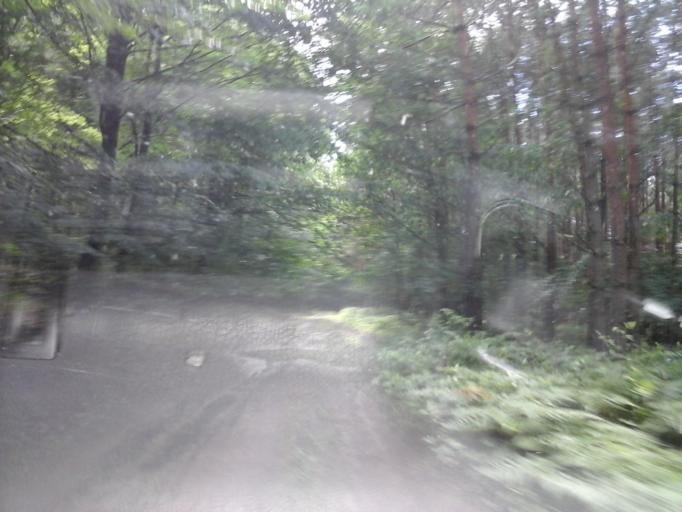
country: PL
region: West Pomeranian Voivodeship
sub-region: Powiat choszczenski
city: Bierzwnik
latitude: 52.9811
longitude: 15.6136
